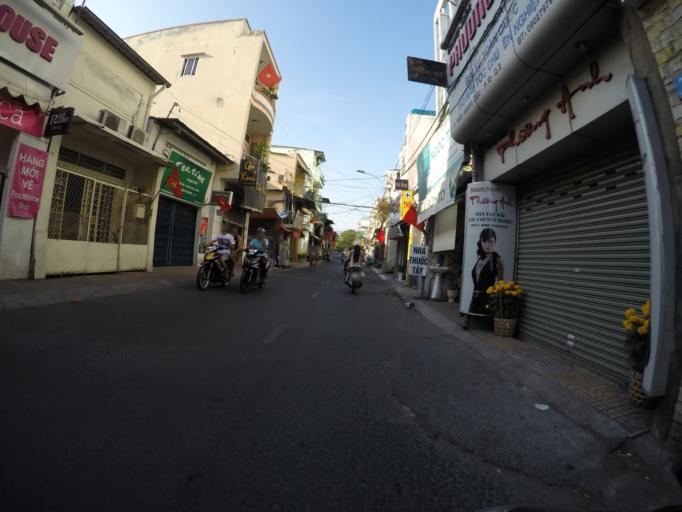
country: VN
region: Ho Chi Minh City
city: Quan Phu Nhuan
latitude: 10.7854
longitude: 106.6785
